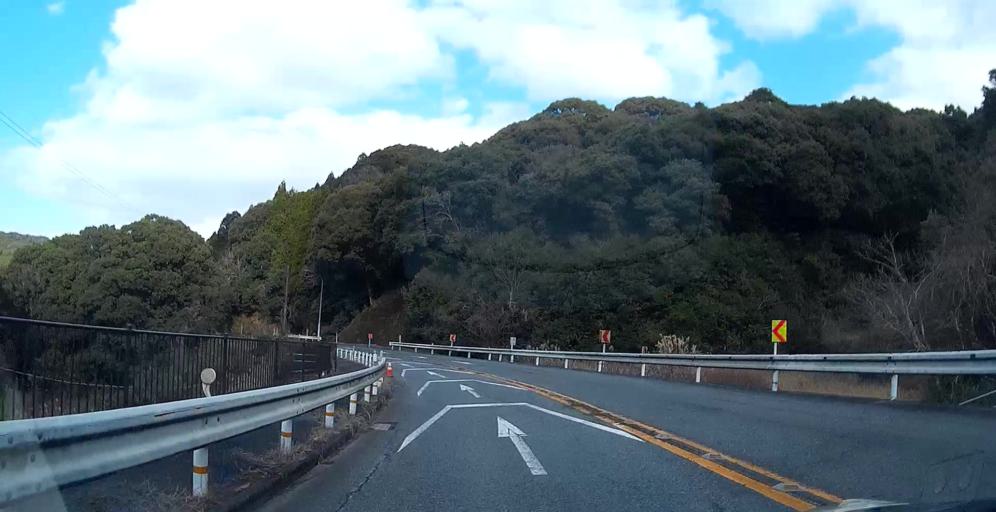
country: JP
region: Kumamoto
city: Yatsushiro
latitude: 32.3866
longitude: 130.5443
